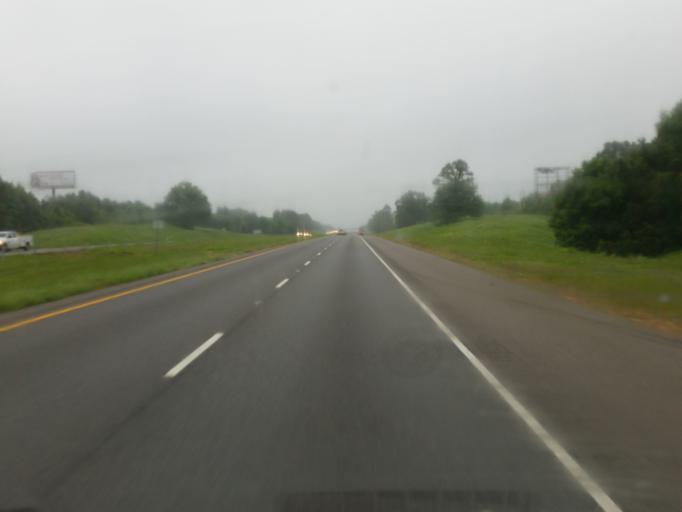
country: US
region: Louisiana
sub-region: Bossier Parish
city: Red Chute
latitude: 32.5418
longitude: -93.6176
